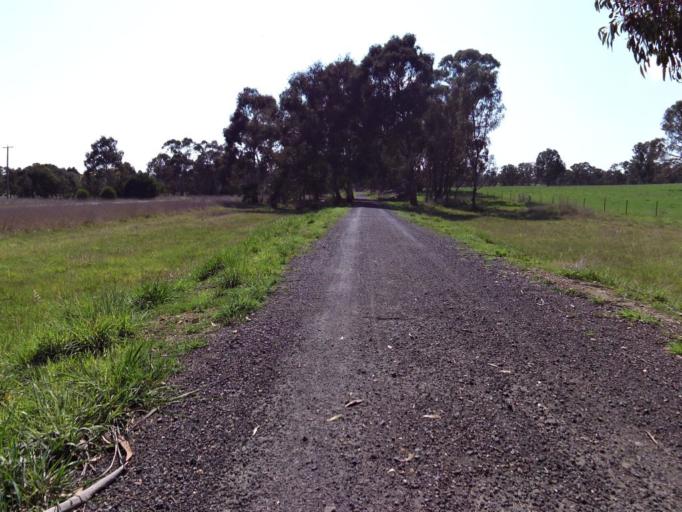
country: AU
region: Victoria
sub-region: Murrindindi
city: Alexandra
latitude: -37.1228
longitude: 145.6008
